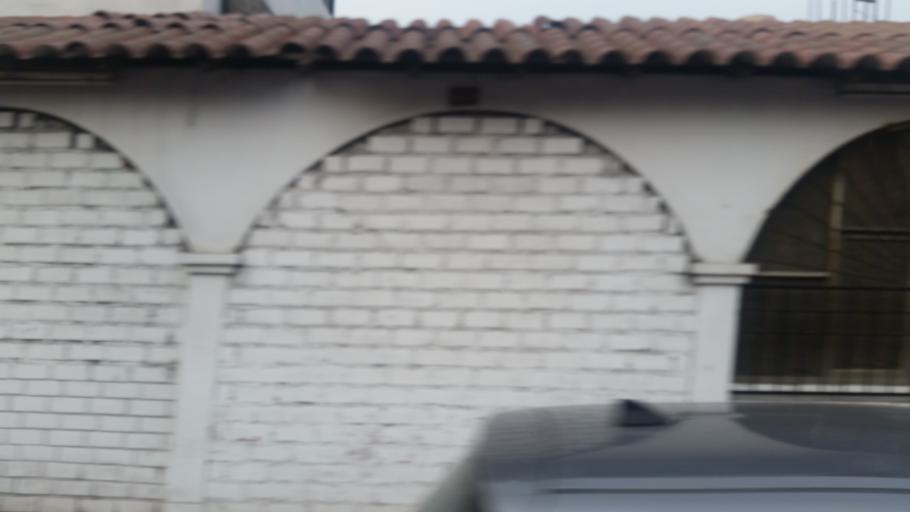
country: PE
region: Lima
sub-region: Lima
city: San Isidro
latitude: -12.0880
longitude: -77.0817
